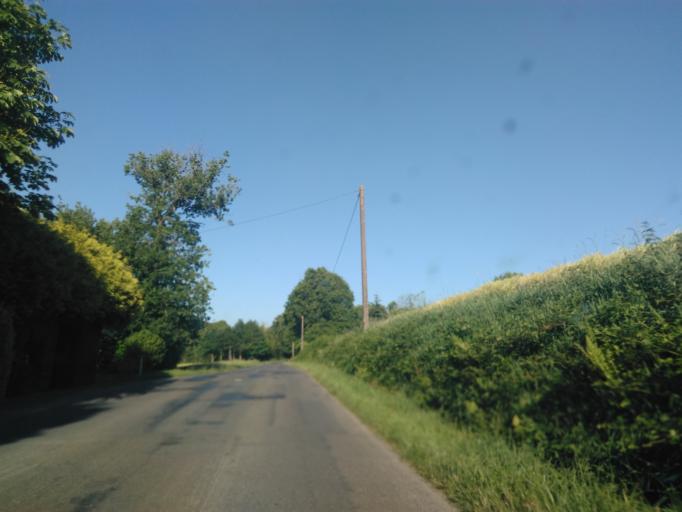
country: FR
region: Brittany
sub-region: Departement d'Ille-et-Vilaine
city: Geveze
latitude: 48.2251
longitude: -1.7761
